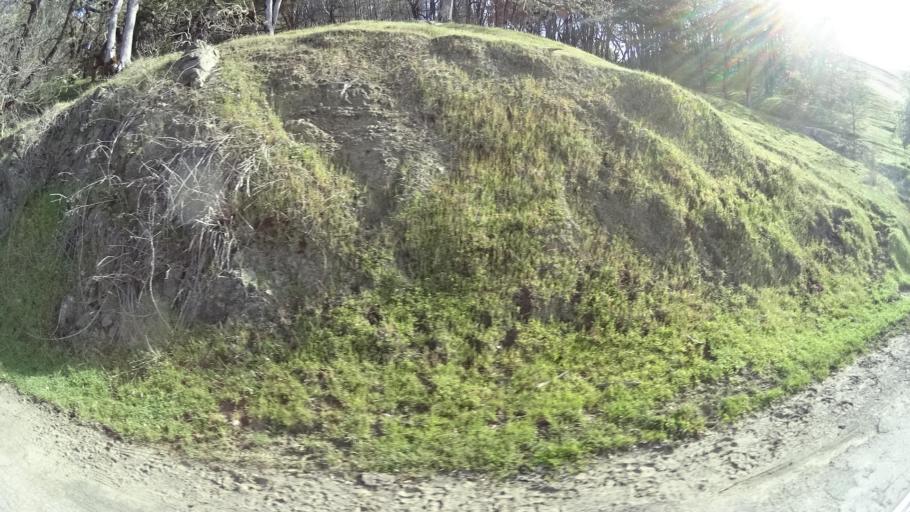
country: US
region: California
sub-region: Humboldt County
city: Hydesville
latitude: 40.6438
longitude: -123.9182
